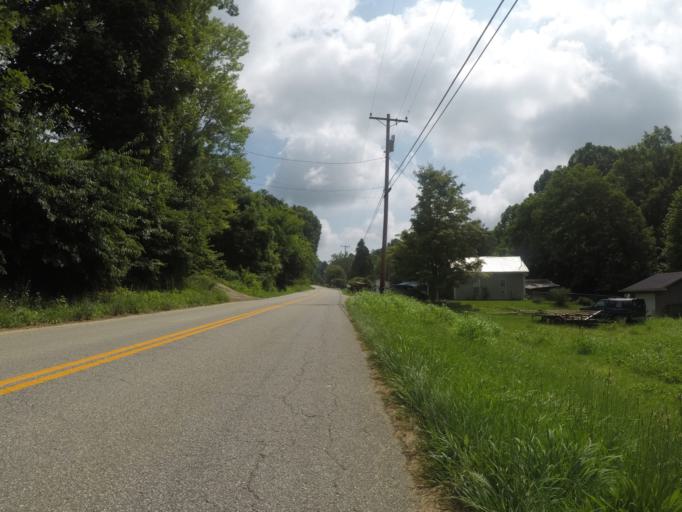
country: US
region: Kentucky
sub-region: Boyd County
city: Catlettsburg
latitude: 38.4012
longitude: -82.6517
